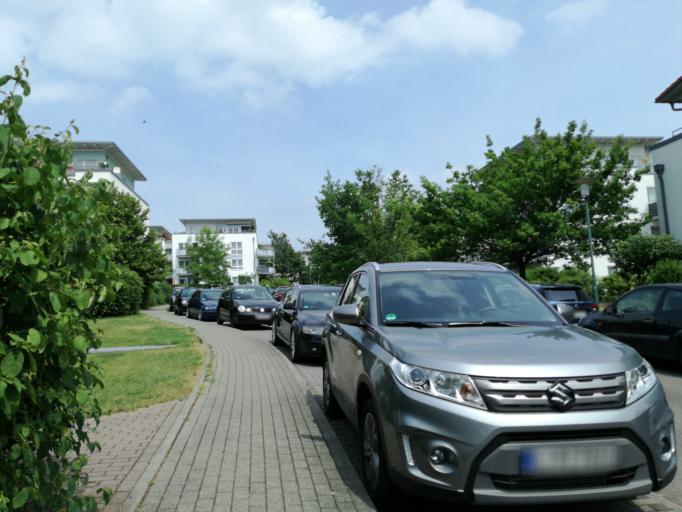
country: DE
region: Saxony
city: Leipzig
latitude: 51.3799
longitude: 12.3282
